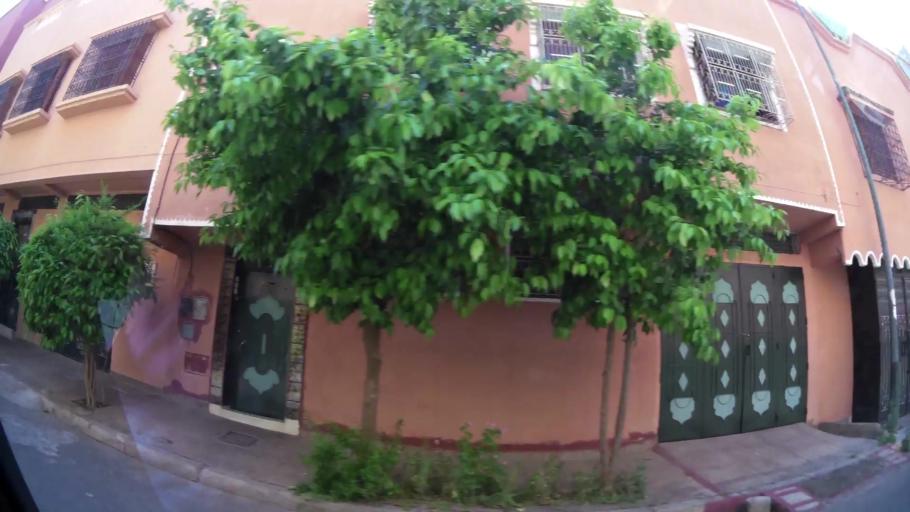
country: MA
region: Marrakech-Tensift-Al Haouz
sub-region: Marrakech
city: Marrakesh
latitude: 31.6604
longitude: -7.9873
